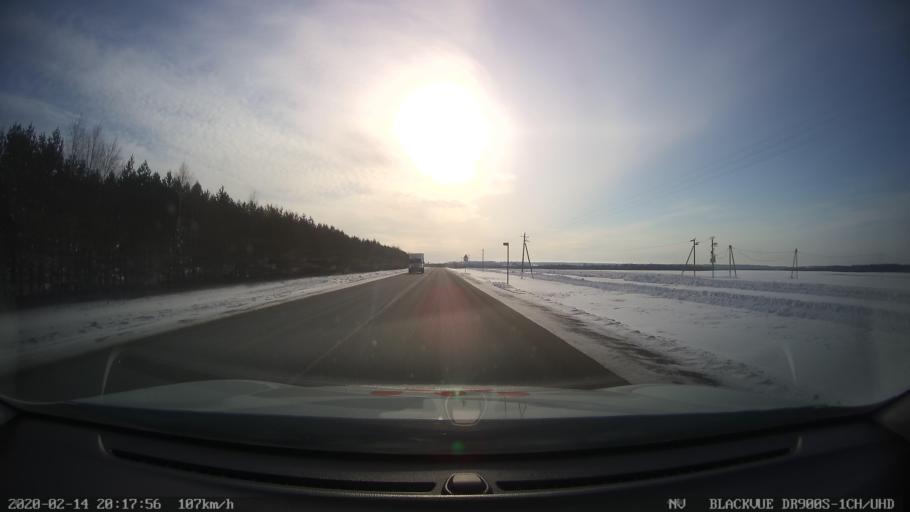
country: RU
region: Tatarstan
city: Verkhniy Uslon
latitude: 55.5931
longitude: 48.8825
